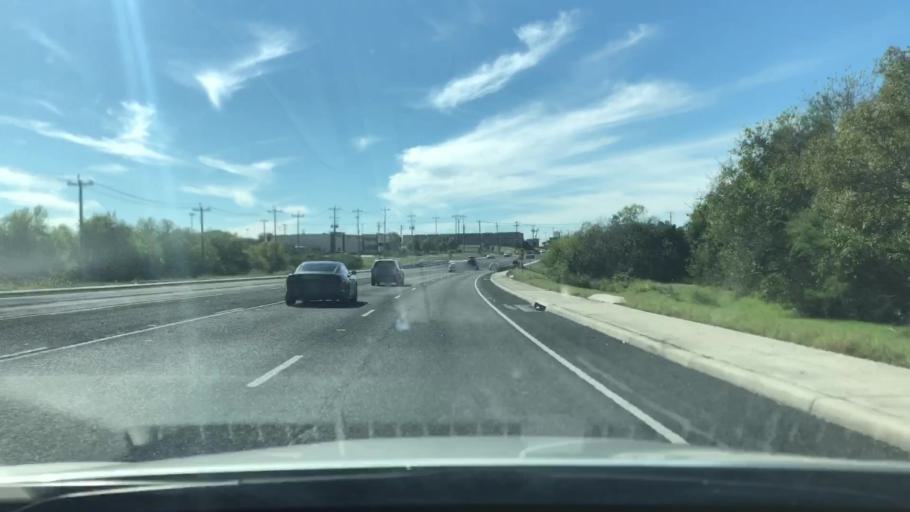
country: US
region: Texas
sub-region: Bexar County
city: Converse
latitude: 29.4867
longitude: -98.3438
